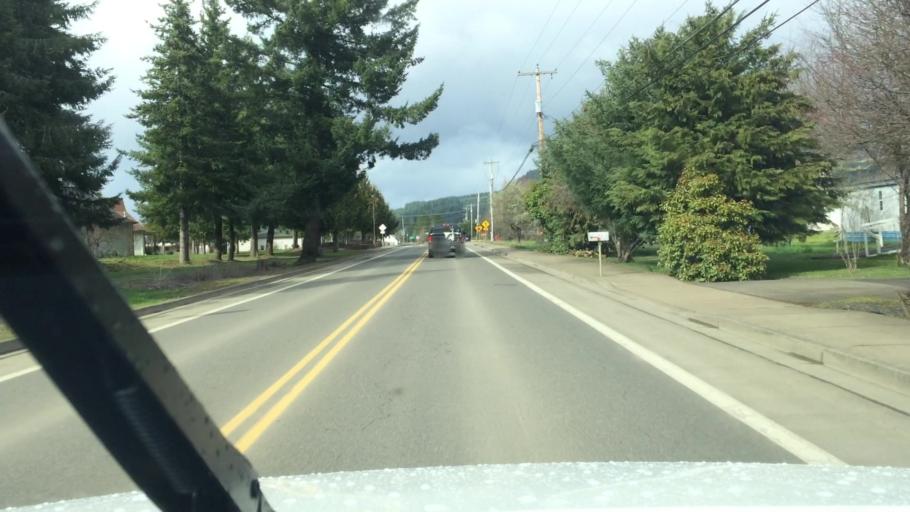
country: US
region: Oregon
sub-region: Polk County
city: Grand Ronde
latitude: 45.0770
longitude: -123.6119
